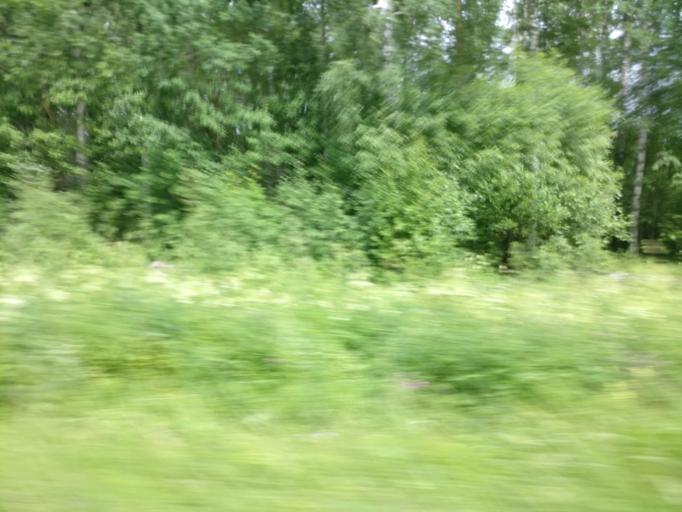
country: FI
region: Southern Savonia
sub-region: Pieksaemaeki
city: Joroinen
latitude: 62.1977
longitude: 27.9964
